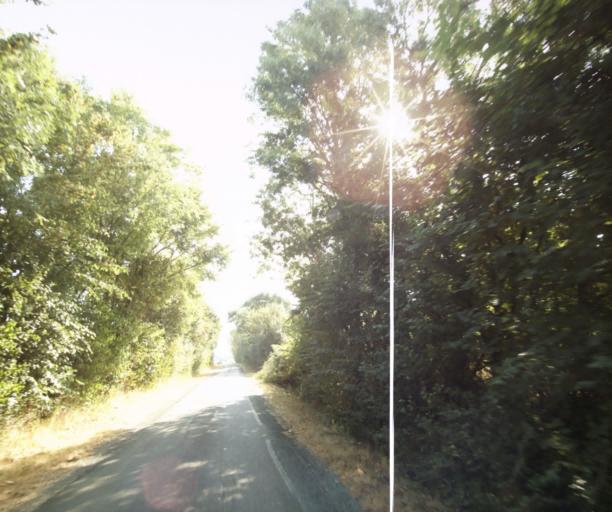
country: FR
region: Poitou-Charentes
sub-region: Departement de la Charente-Maritime
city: Tonnay-Charente
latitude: 45.9661
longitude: -0.8665
